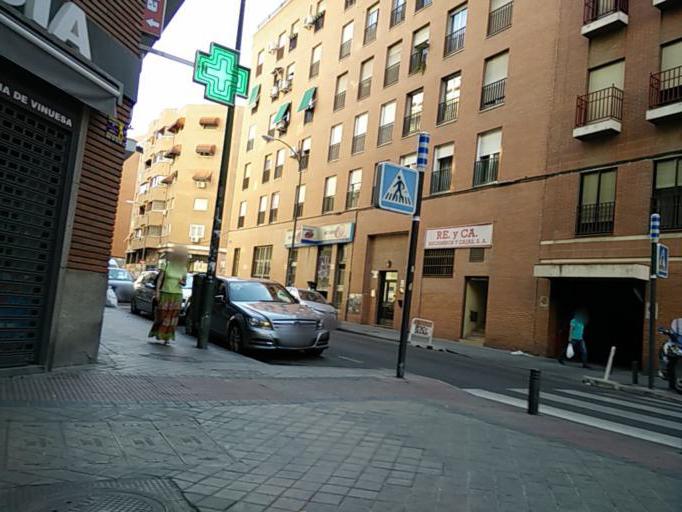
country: ES
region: Madrid
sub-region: Provincia de Madrid
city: Madrid
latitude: 40.4109
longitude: -3.7195
